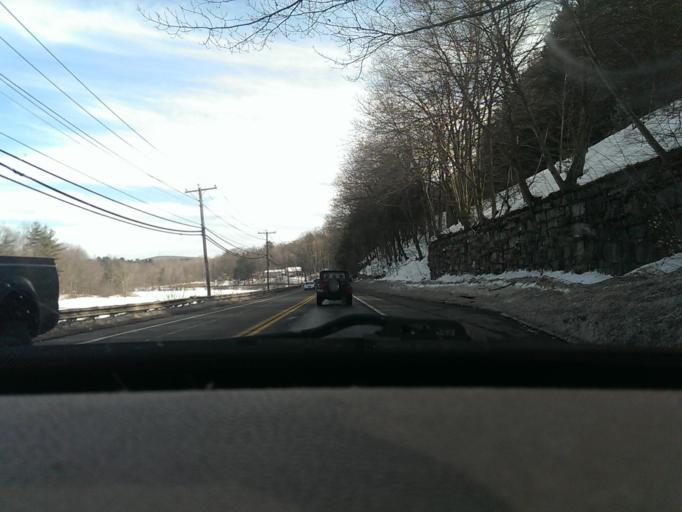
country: US
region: Massachusetts
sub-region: Hampden County
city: Wilbraham
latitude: 42.1538
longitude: -72.4170
